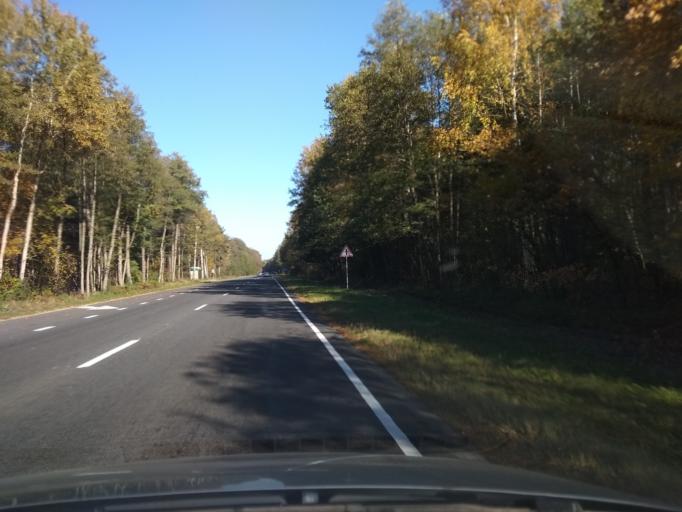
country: BY
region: Brest
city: Kobryn
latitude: 52.0583
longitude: 24.2812
